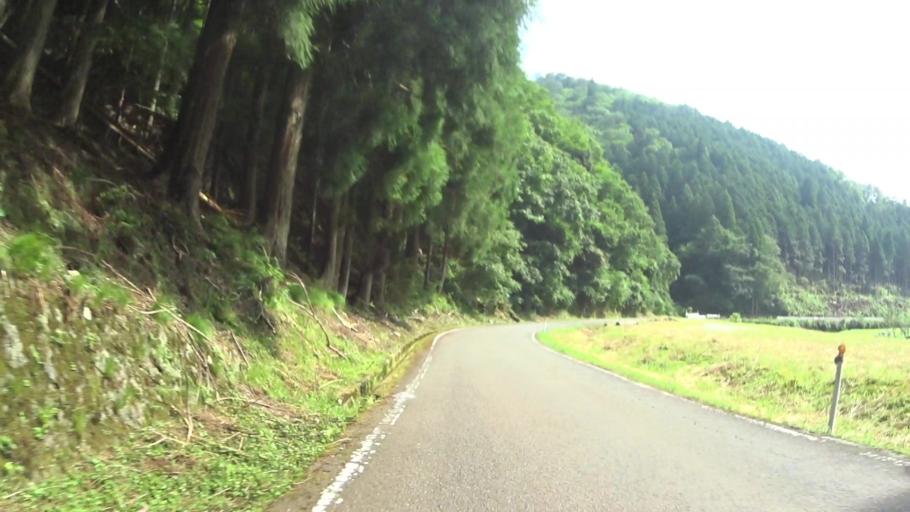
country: JP
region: Fukui
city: Obama
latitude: 35.3288
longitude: 135.6462
